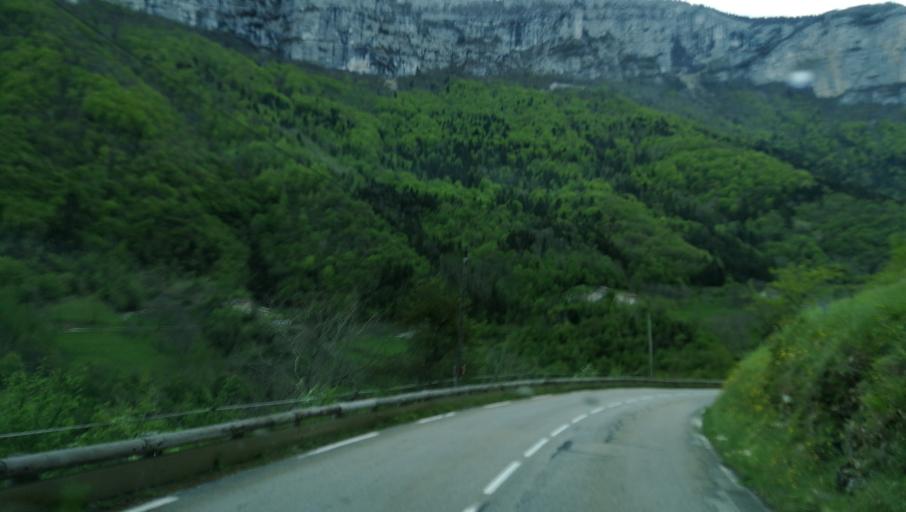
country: FR
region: Rhone-Alpes
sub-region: Departement de l'Isere
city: Pont-en-Royans
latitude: 45.0593
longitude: 5.4111
